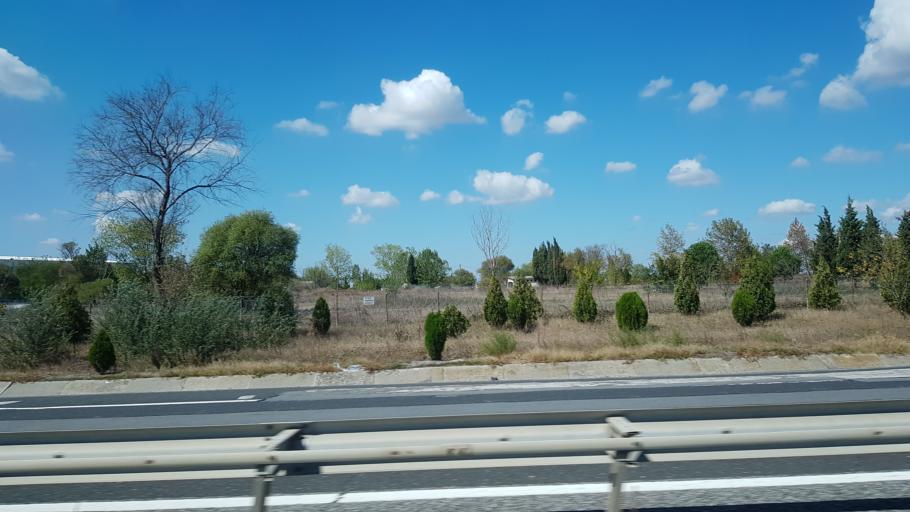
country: TR
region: Tekirdag
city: Velimese
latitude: 41.2244
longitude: 27.8726
